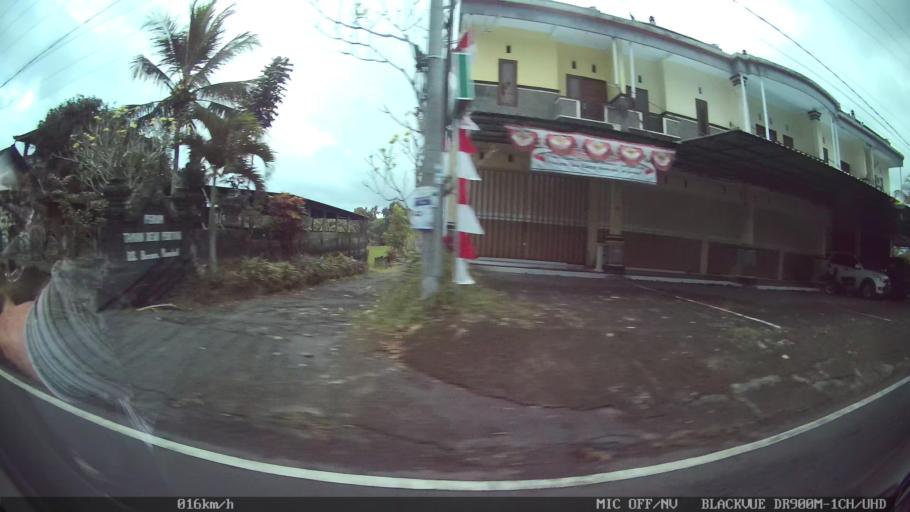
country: ID
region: Bali
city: Pohgending Kawan
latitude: -8.4420
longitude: 115.1412
